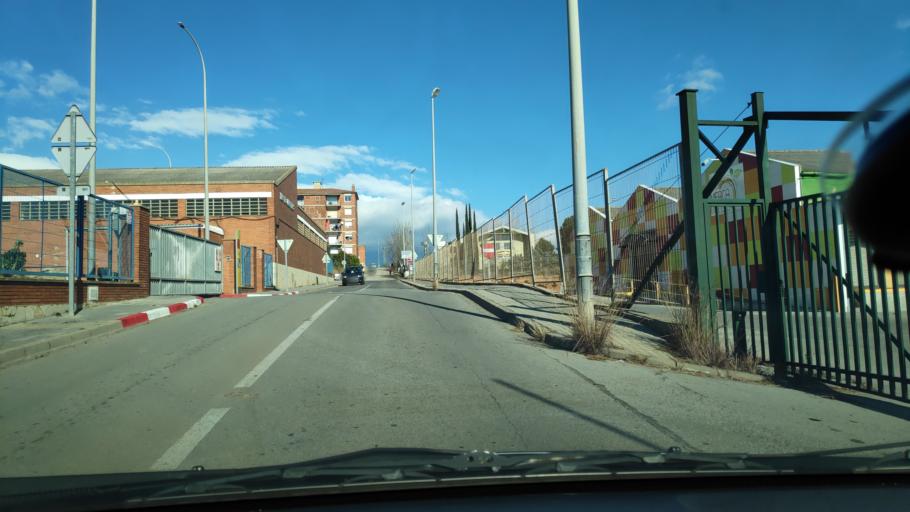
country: ES
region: Catalonia
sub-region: Provincia de Barcelona
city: Sant Quirze del Valles
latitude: 41.5538
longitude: 2.0590
